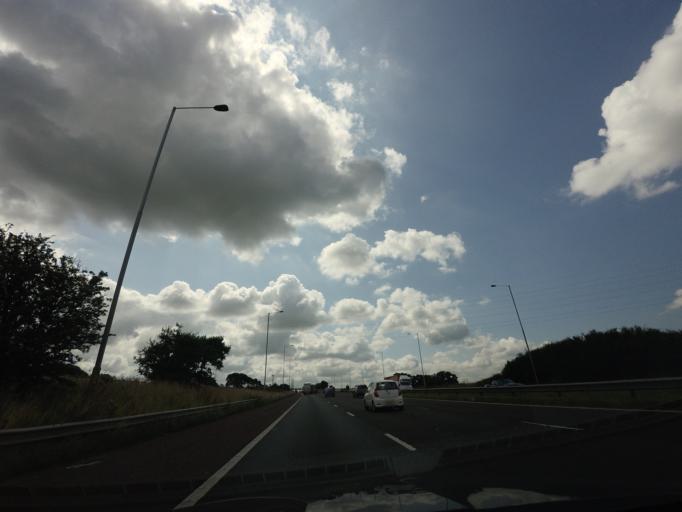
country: GB
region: England
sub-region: Lancashire
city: Euxton
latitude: 53.6483
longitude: -2.6916
